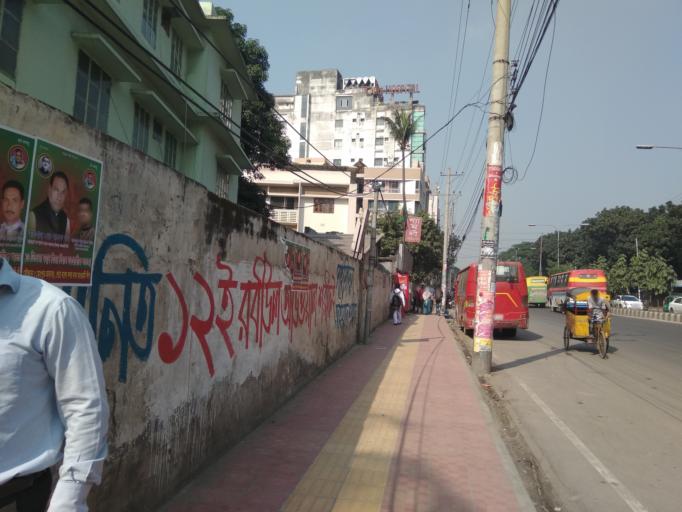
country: BD
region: Dhaka
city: Azimpur
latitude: 23.7614
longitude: 90.3722
